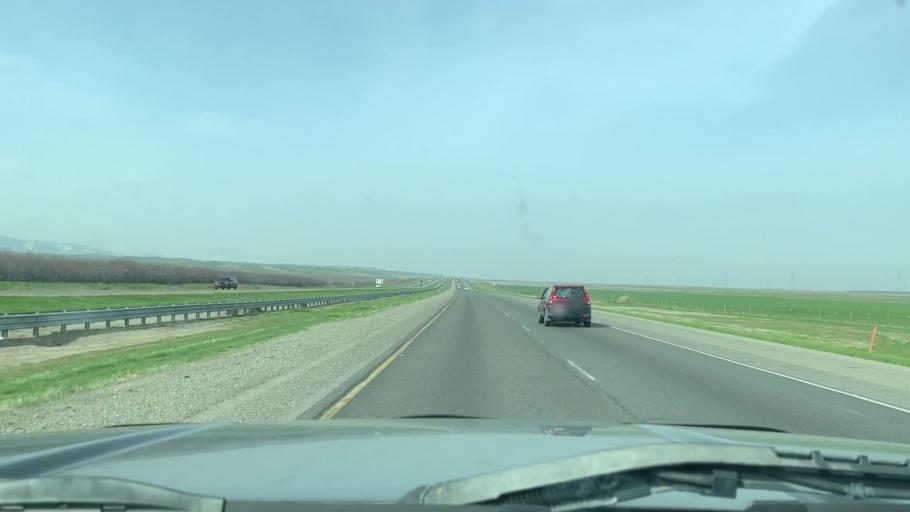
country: US
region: California
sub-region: Fresno County
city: San Joaquin
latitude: 36.4510
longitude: -120.4077
